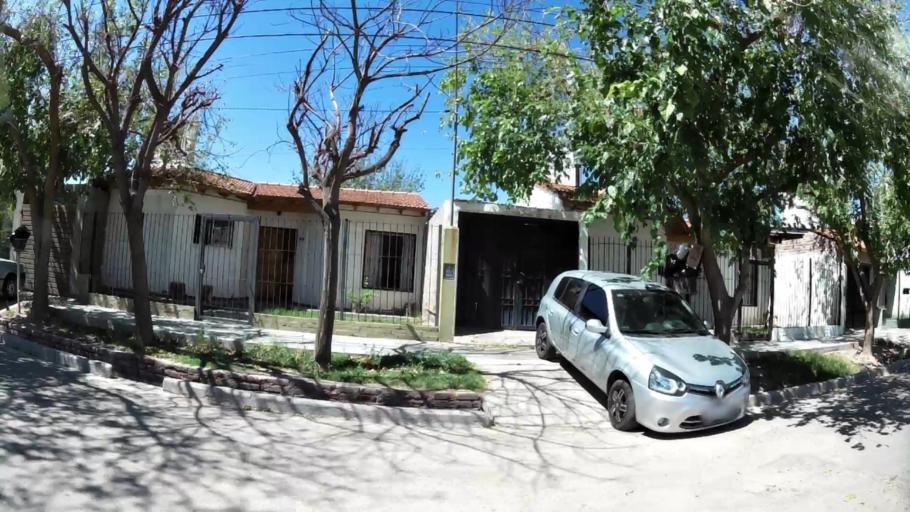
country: AR
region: Mendoza
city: Las Heras
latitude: -32.8510
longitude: -68.8533
